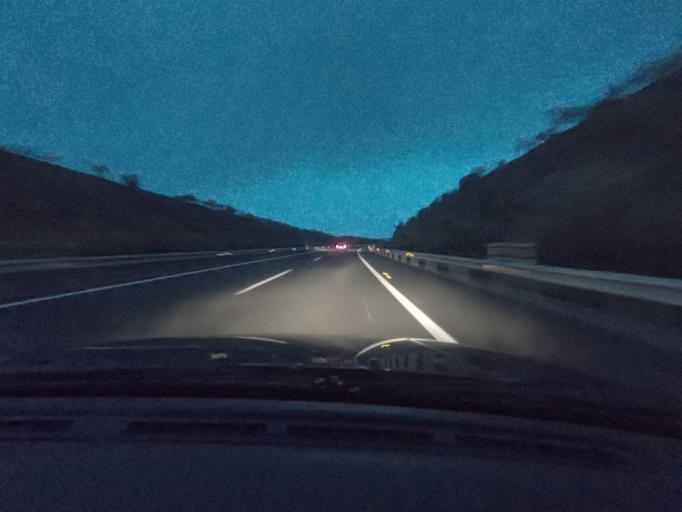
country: ES
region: Extremadura
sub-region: Provincia de Caceres
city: Aldea del Cano
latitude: 39.3417
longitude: -6.3407
